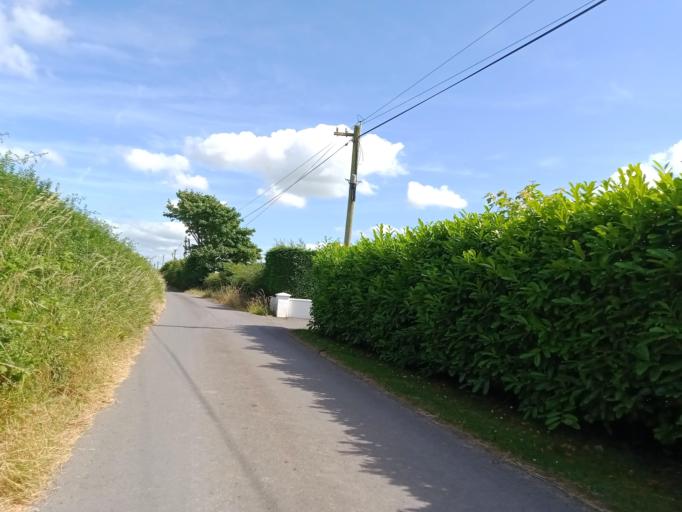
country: IE
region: Leinster
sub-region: Kilkenny
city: Kilkenny
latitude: 52.6367
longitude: -7.2103
